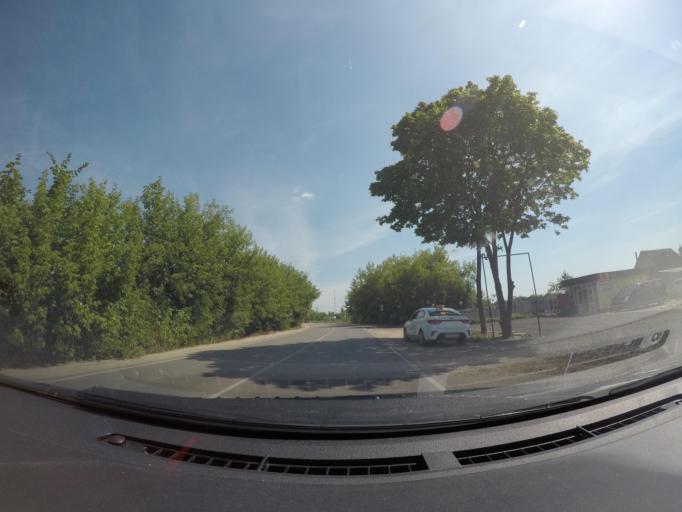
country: RU
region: Moskovskaya
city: Rechitsy
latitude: 55.6082
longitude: 38.4461
